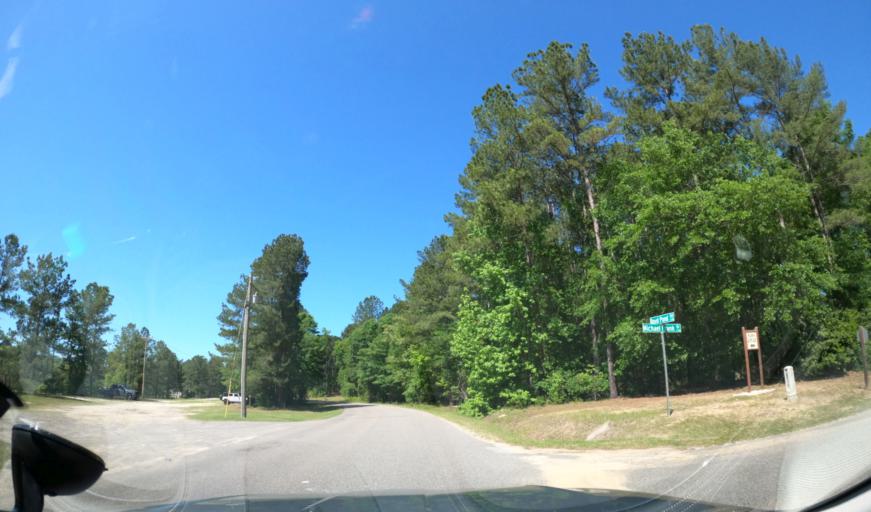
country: US
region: South Carolina
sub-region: Aiken County
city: Langley
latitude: 33.4517
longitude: -81.7964
